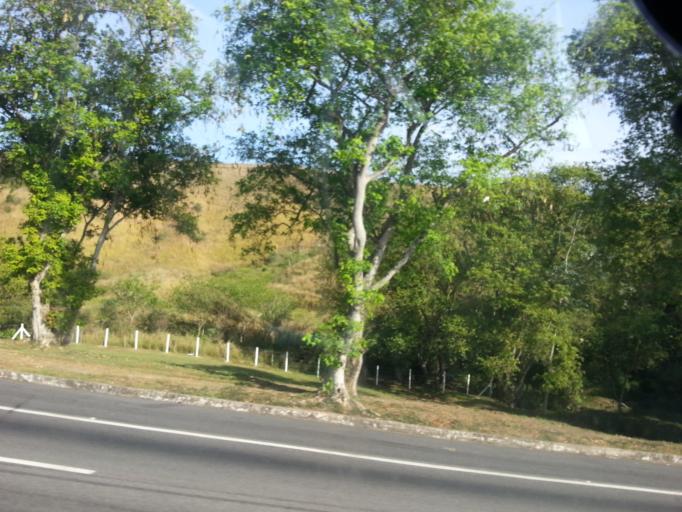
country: BR
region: Rio de Janeiro
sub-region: Volta Redonda
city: Volta Redonda
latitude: -22.5621
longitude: -44.1219
